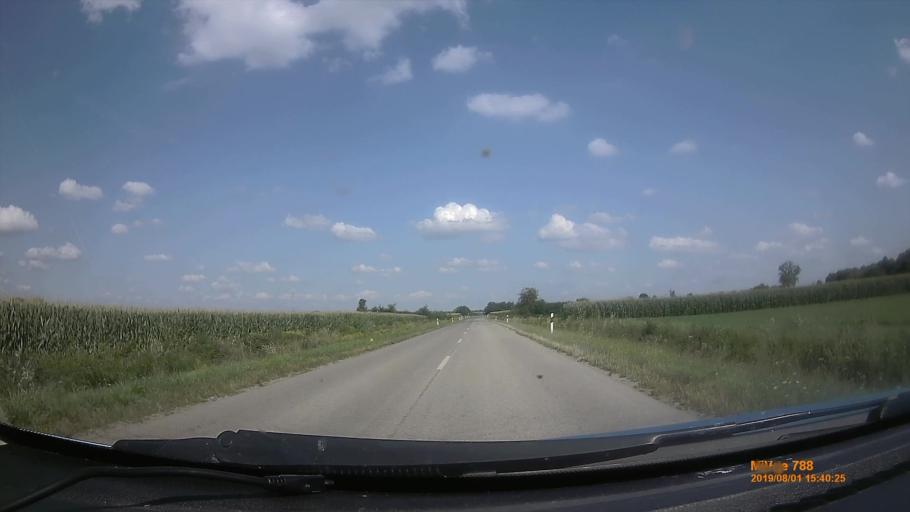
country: HU
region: Baranya
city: Szentlorinc
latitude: 45.9877
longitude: 17.9522
